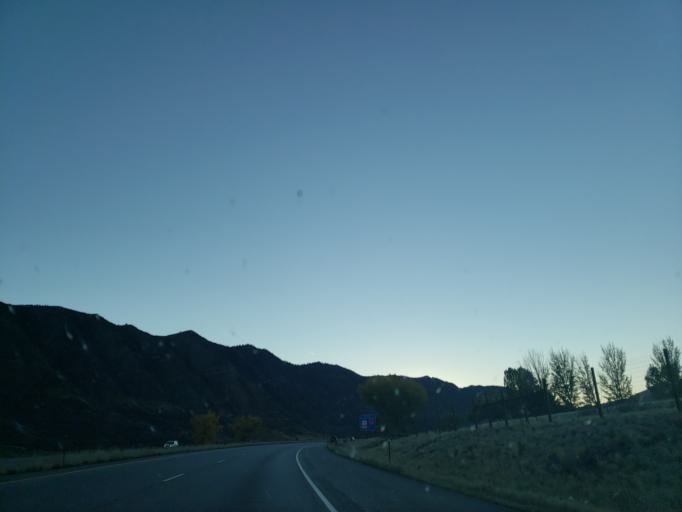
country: US
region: Colorado
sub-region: Garfield County
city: New Castle
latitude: 39.5669
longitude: -107.4894
